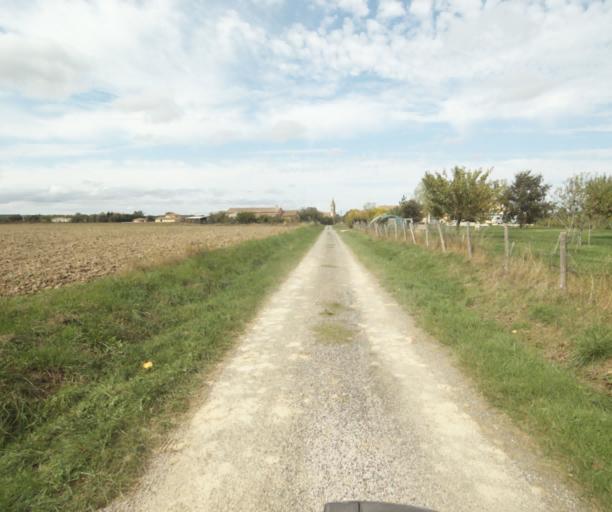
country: FR
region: Midi-Pyrenees
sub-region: Departement du Tarn-et-Garonne
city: Verdun-sur-Garonne
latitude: 43.8601
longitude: 1.1795
